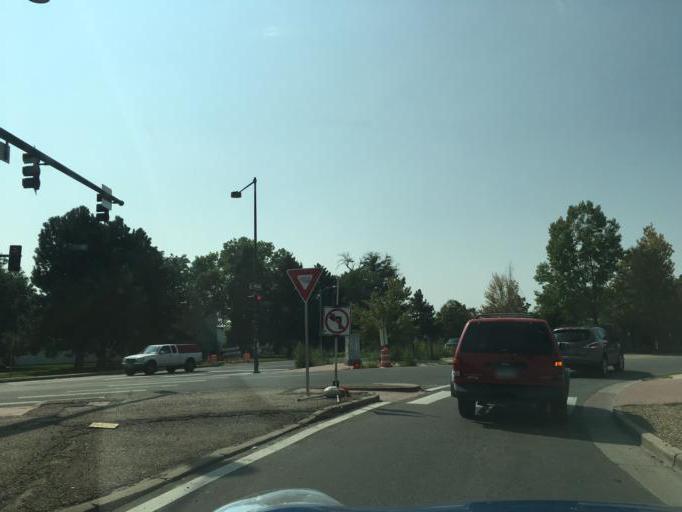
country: US
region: Colorado
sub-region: Denver County
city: Denver
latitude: 39.7703
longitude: -104.9723
